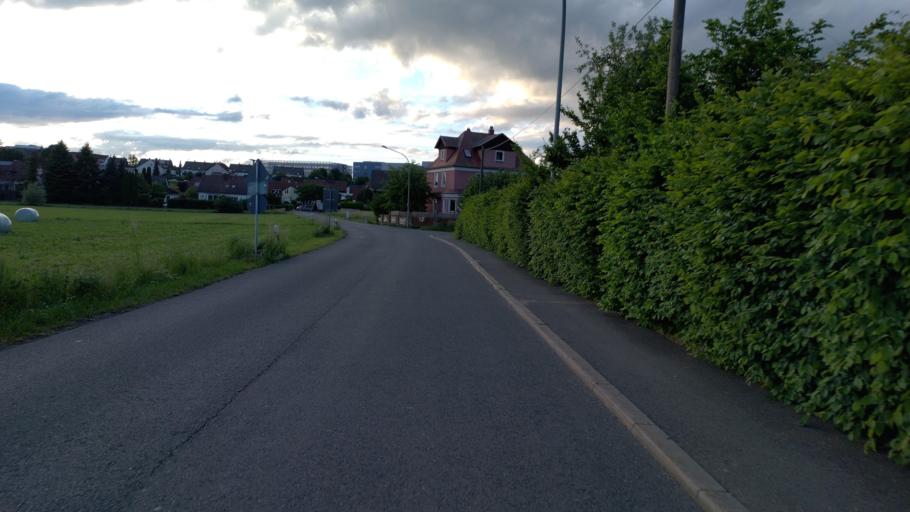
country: DE
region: Bavaria
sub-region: Upper Franconia
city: Bindlach
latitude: 49.9542
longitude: 11.6157
